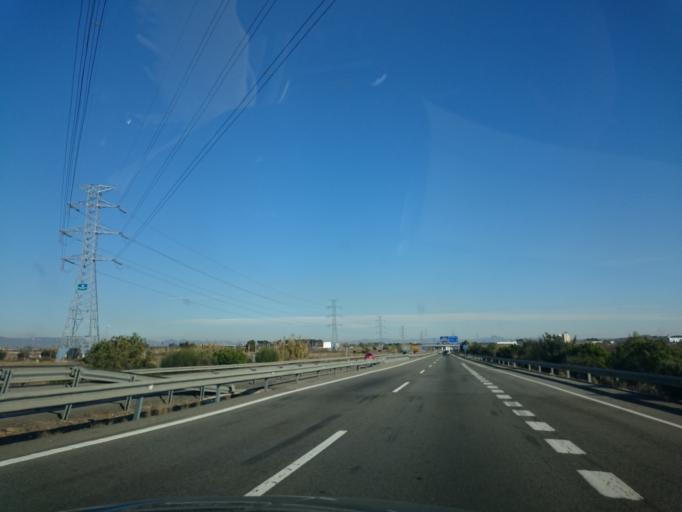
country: ES
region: Catalonia
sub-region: Provincia de Tarragona
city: Vila-seca
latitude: 41.1223
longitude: 1.1627
